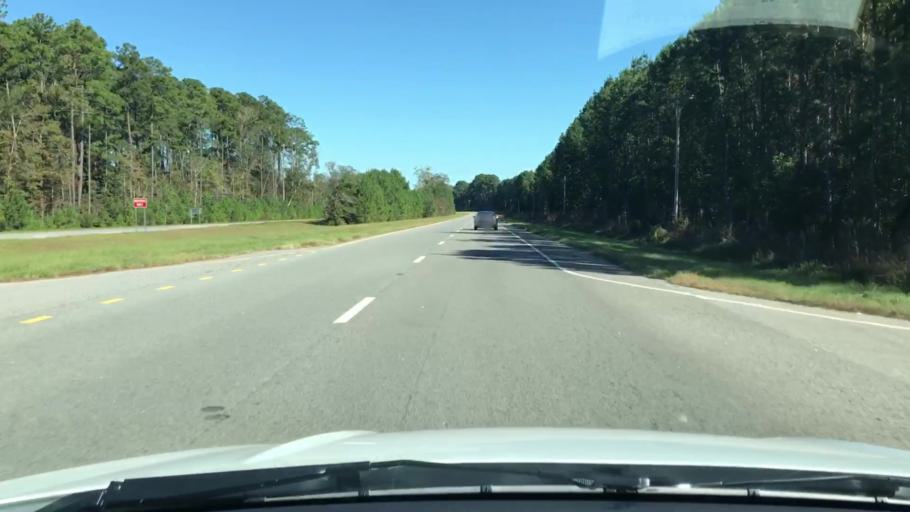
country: US
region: South Carolina
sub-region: Colleton County
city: Walterboro
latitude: 32.7374
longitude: -80.5745
